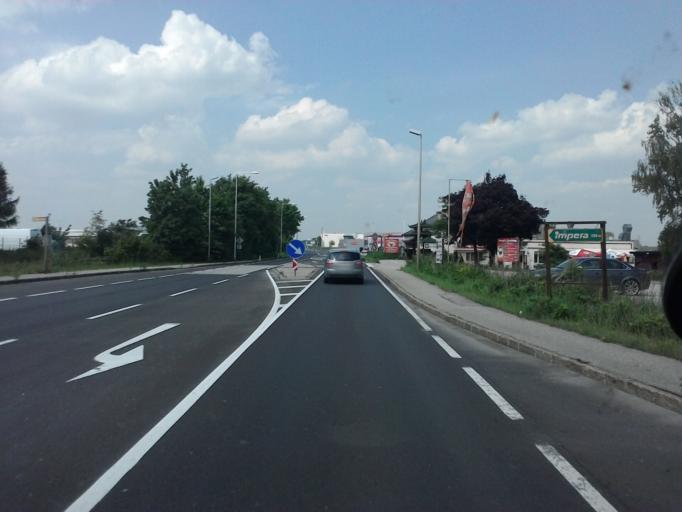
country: AT
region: Upper Austria
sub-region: Wels-Land
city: Steinhaus
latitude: 48.1025
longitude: 14.0396
